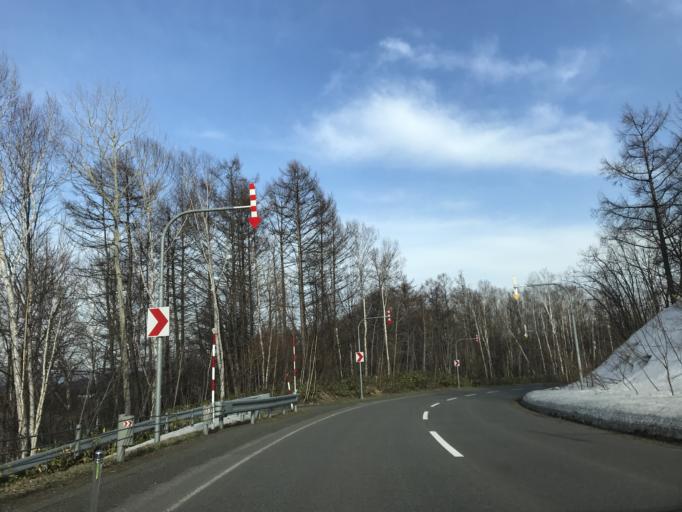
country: JP
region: Hokkaido
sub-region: Asahikawa-shi
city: Asahikawa
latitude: 43.6977
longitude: 142.3288
